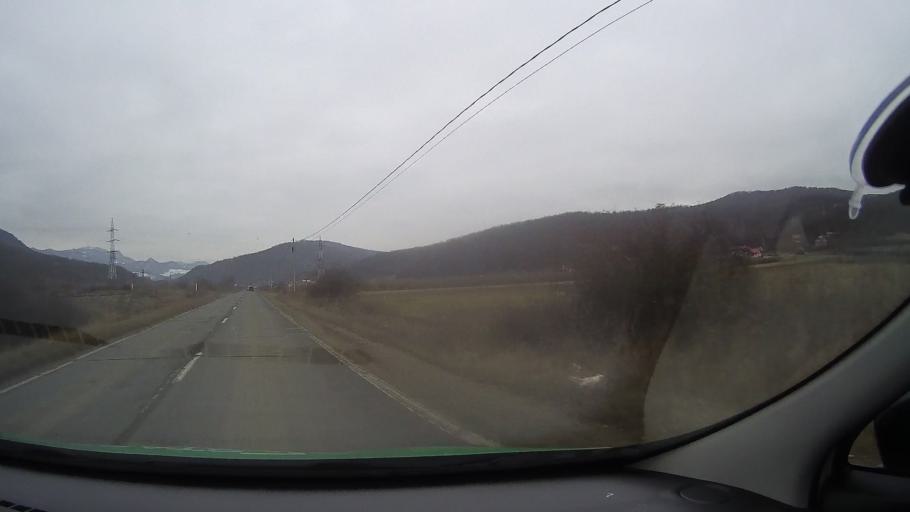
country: RO
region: Alba
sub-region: Comuna Ighiu
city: Ighiel
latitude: 46.1151
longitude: 23.4945
